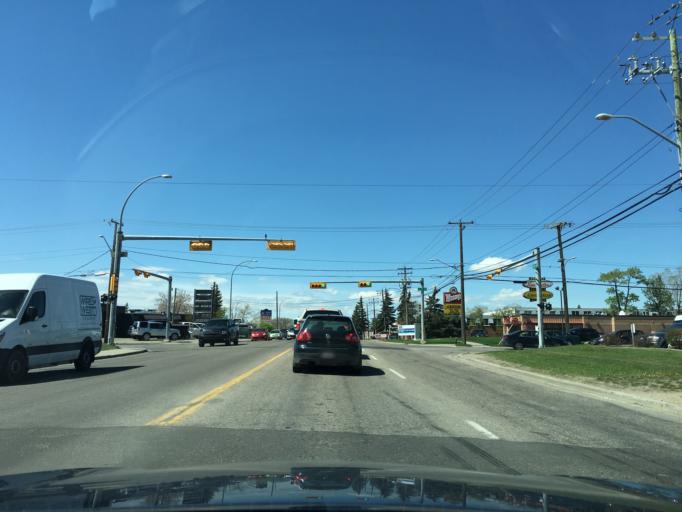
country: CA
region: Alberta
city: Calgary
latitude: 51.0014
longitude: -114.0531
